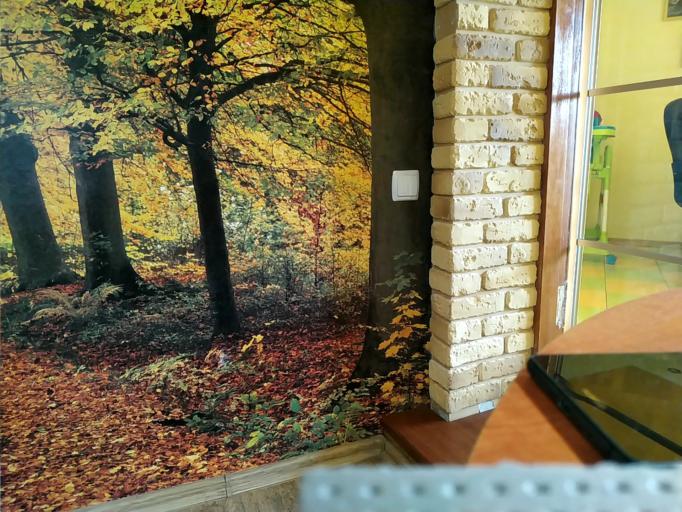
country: RU
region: Tverskaya
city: Zubtsov
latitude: 56.2220
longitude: 34.5291
